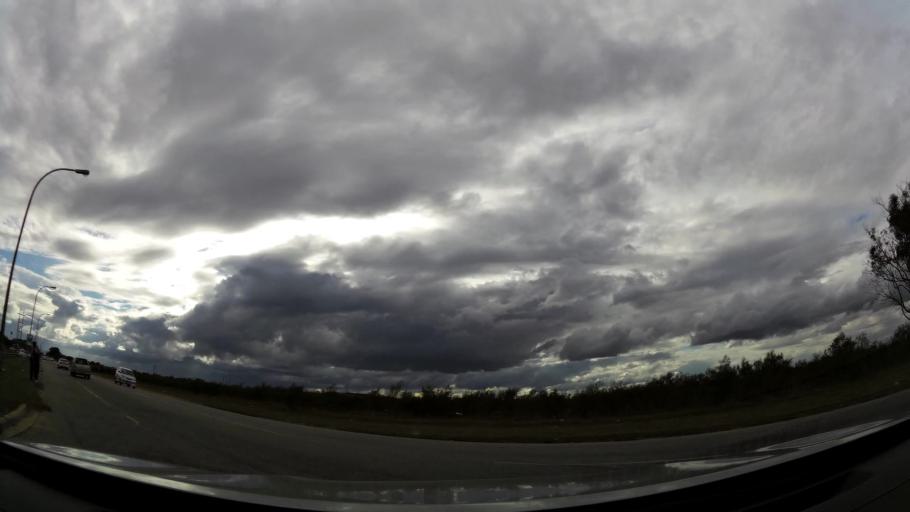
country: ZA
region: Eastern Cape
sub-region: Nelson Mandela Bay Metropolitan Municipality
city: Port Elizabeth
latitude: -33.9357
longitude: 25.4740
